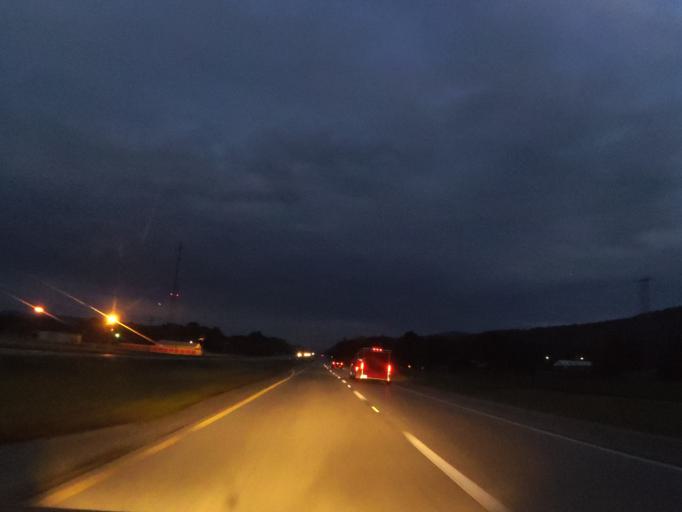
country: US
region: Alabama
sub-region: Jackson County
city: Scottsboro
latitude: 34.6217
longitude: -86.1680
